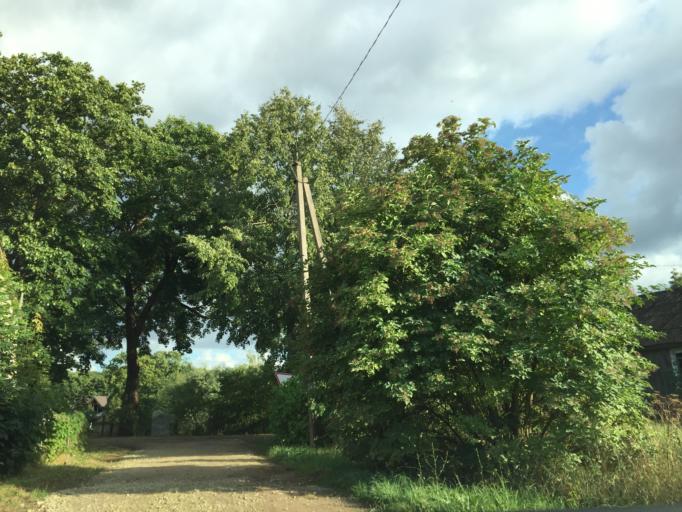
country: LT
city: Zagare
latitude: 56.3642
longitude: 23.2577
